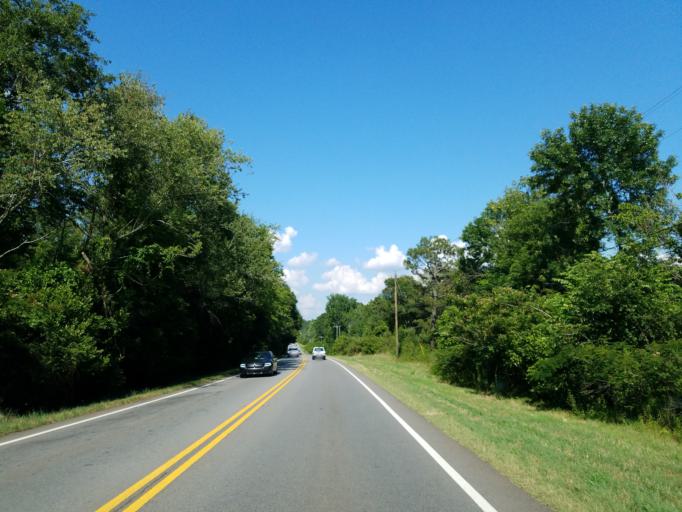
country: US
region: Georgia
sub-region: Peach County
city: Fort Valley
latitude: 32.5541
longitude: -83.8646
